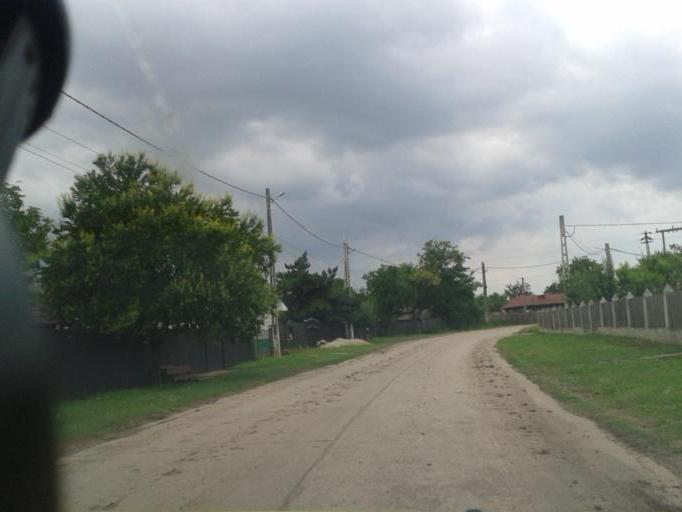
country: RO
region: Ialomita
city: Dragoesti-Snagov
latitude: 44.5334
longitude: 26.4820
